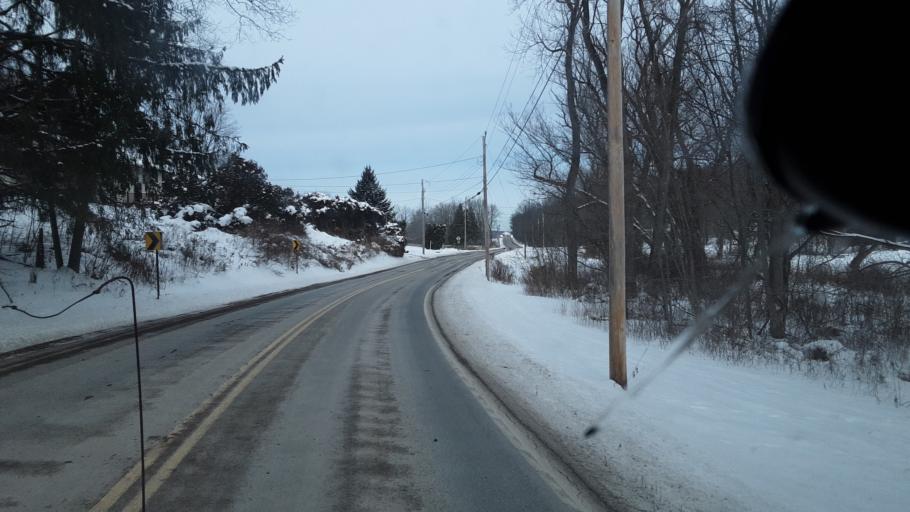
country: US
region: New York
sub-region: Wayne County
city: Newark
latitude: 43.0681
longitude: -77.0564
